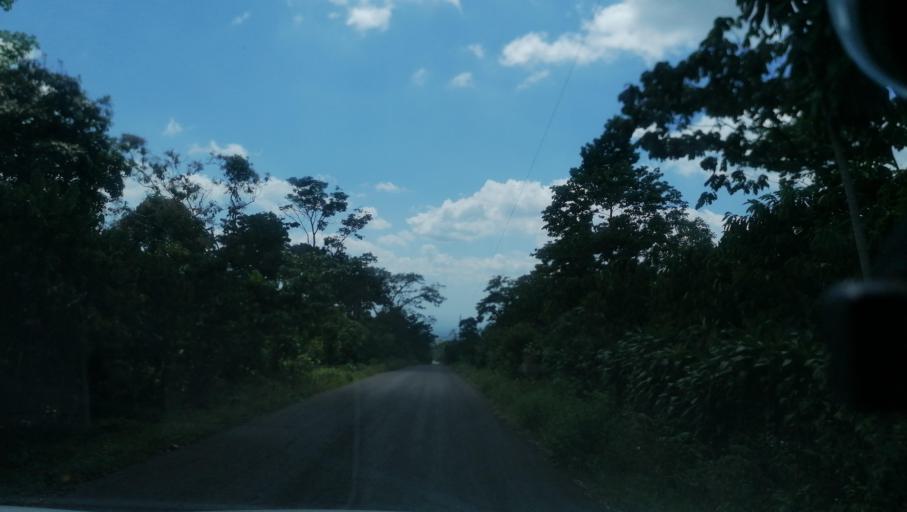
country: MX
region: Chiapas
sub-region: Cacahoatan
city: Benito Juarez
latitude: 15.0566
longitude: -92.1472
